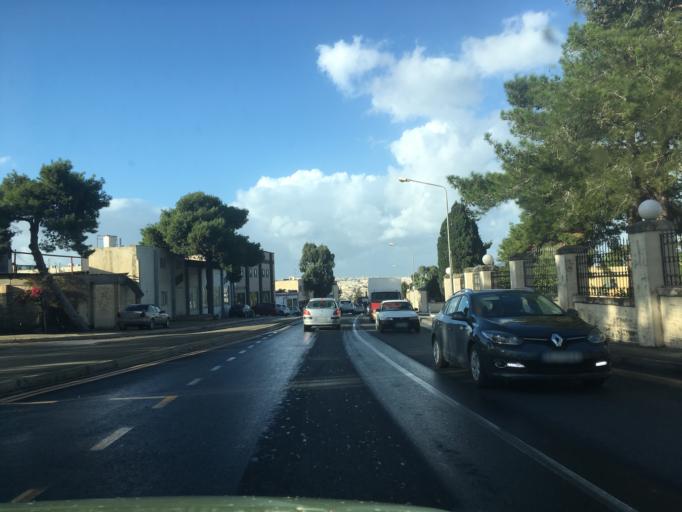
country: MT
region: Luqa
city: Luqa
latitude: 35.8644
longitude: 14.4819
